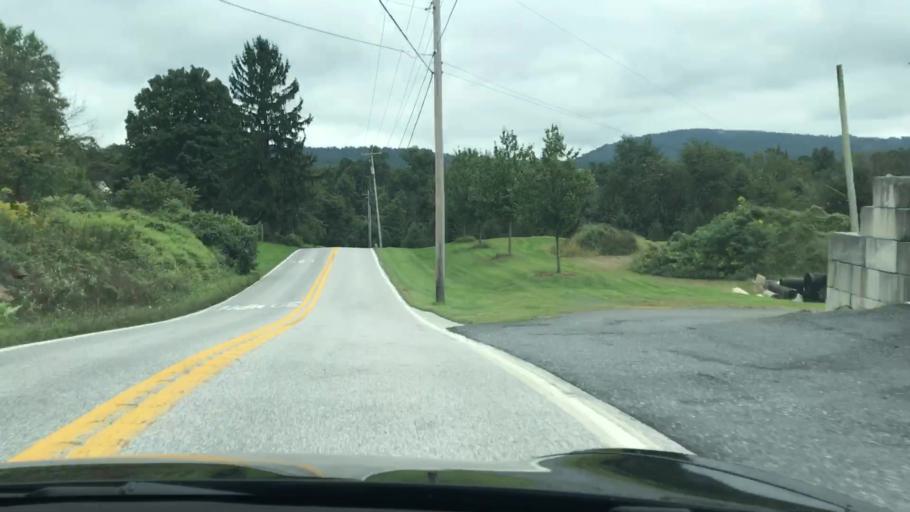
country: US
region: Pennsylvania
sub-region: York County
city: Dillsburg
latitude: 40.1356
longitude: -76.9626
